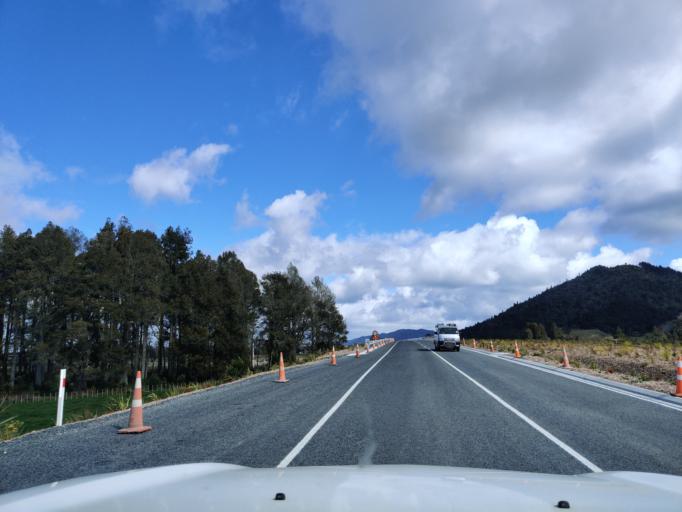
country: NZ
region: Waikato
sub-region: Waikato District
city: Ngaruawahia
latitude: -37.5951
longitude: 175.2066
